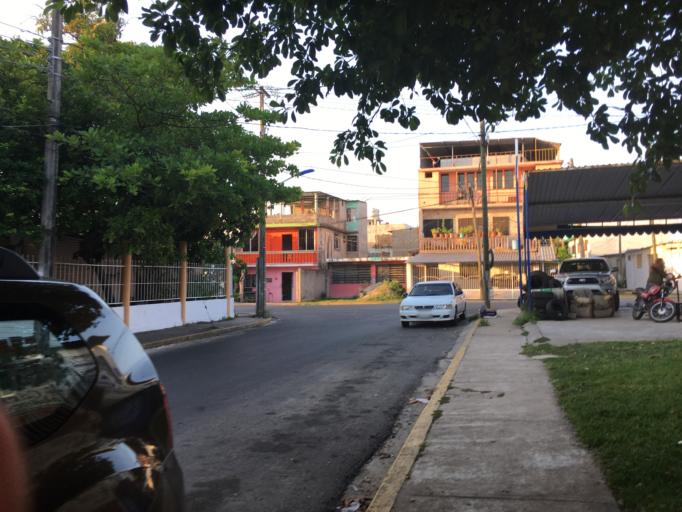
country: MX
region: Tabasco
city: Villahermosa
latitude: 17.9718
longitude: -92.9538
